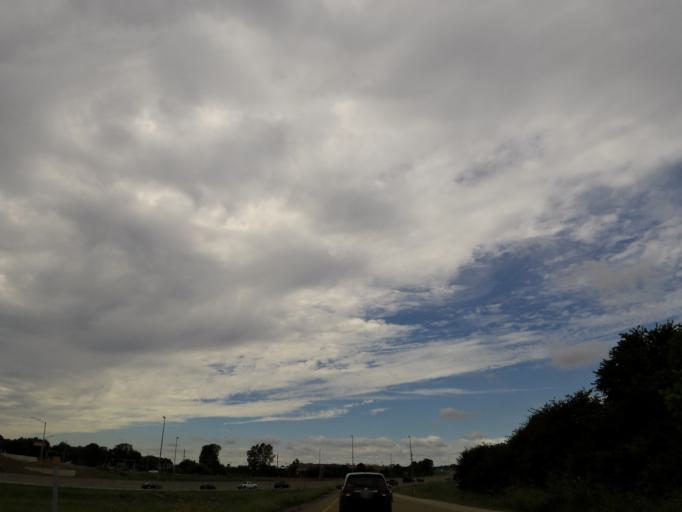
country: US
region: Illinois
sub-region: Saint Clair County
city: O'Fallon
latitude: 38.5933
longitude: -89.9434
